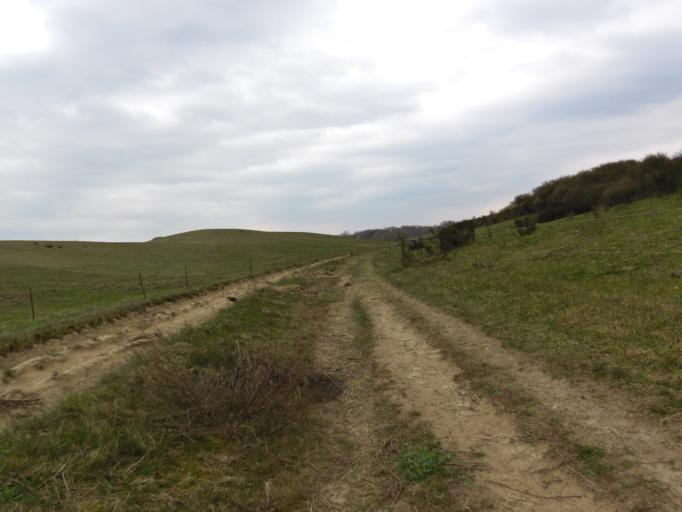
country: DE
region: Mecklenburg-Vorpommern
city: Hiddensee
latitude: 54.5931
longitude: 13.1216
